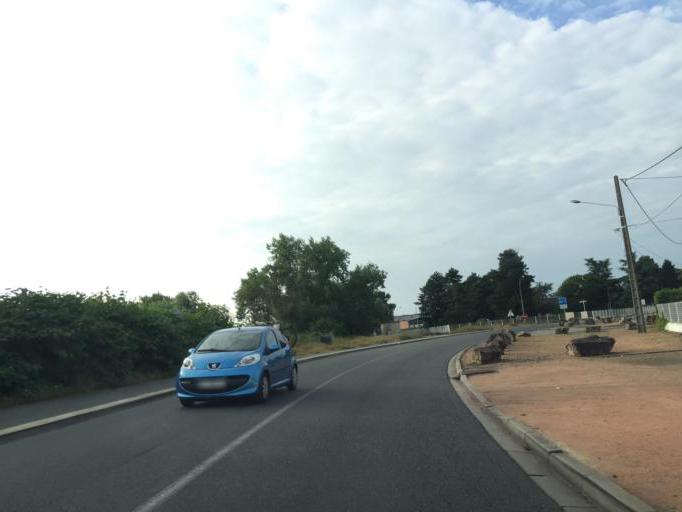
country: FR
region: Auvergne
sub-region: Departement de l'Allier
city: Creuzier-le-Vieux
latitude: 46.1548
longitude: 3.4106
